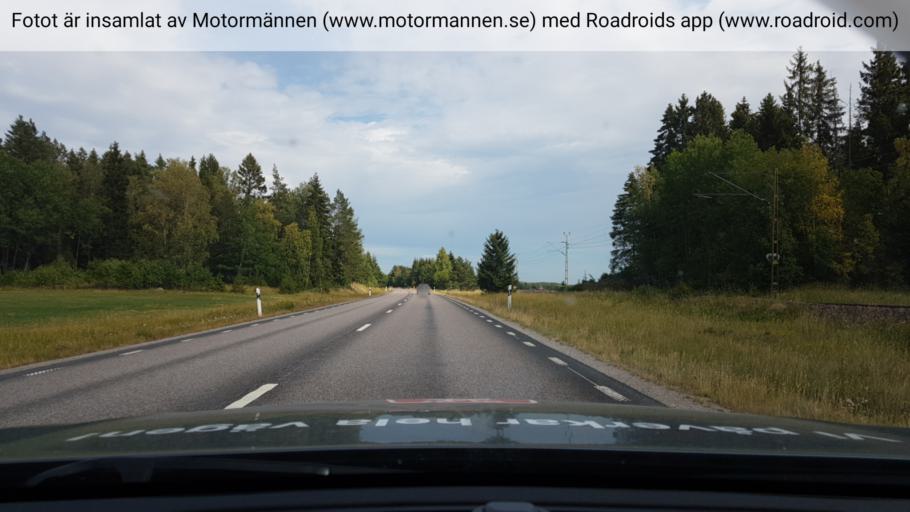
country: SE
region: Uppsala
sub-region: Enkopings Kommun
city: Orsundsbro
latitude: 59.8643
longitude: 17.3438
